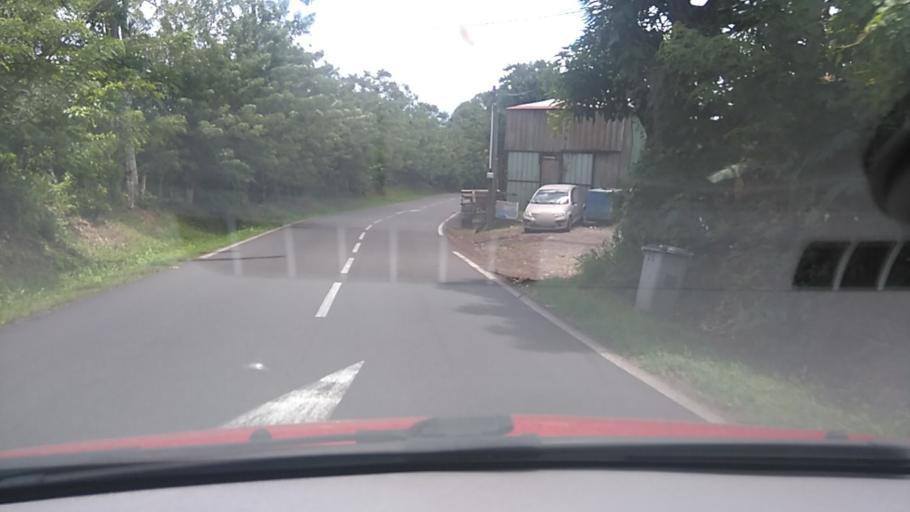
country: MQ
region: Martinique
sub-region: Martinique
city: Ducos
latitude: 14.5696
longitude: -60.9510
